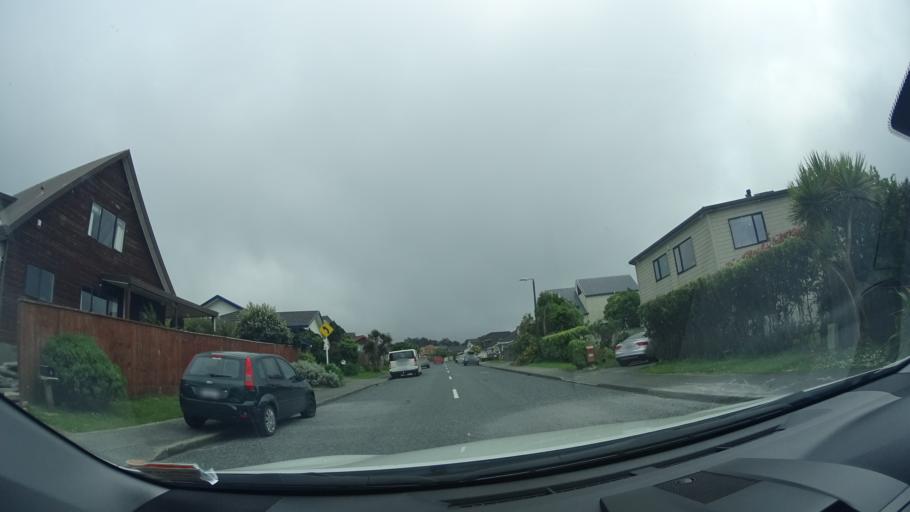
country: NZ
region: Wellington
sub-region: Wellington City
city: Brooklyn
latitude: -41.3040
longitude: 174.7570
